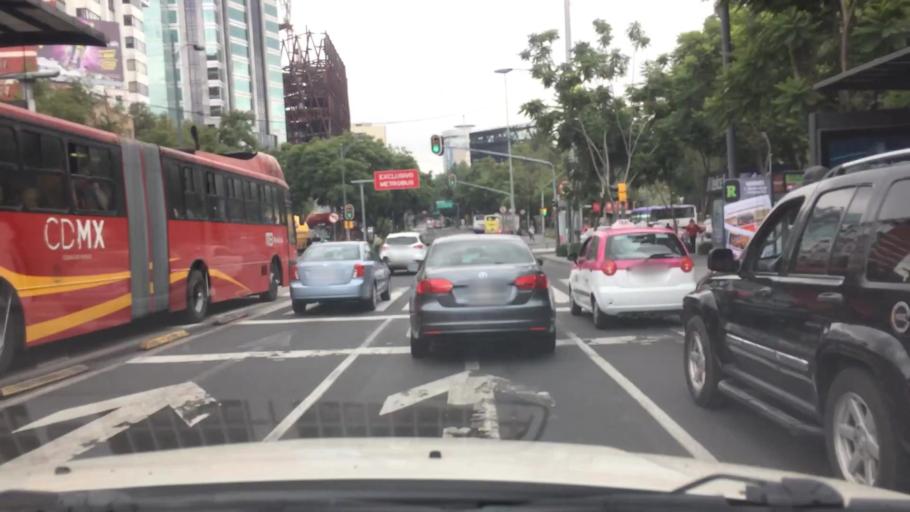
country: MX
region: Mexico City
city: Alvaro Obregon
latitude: 19.3470
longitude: -99.1876
